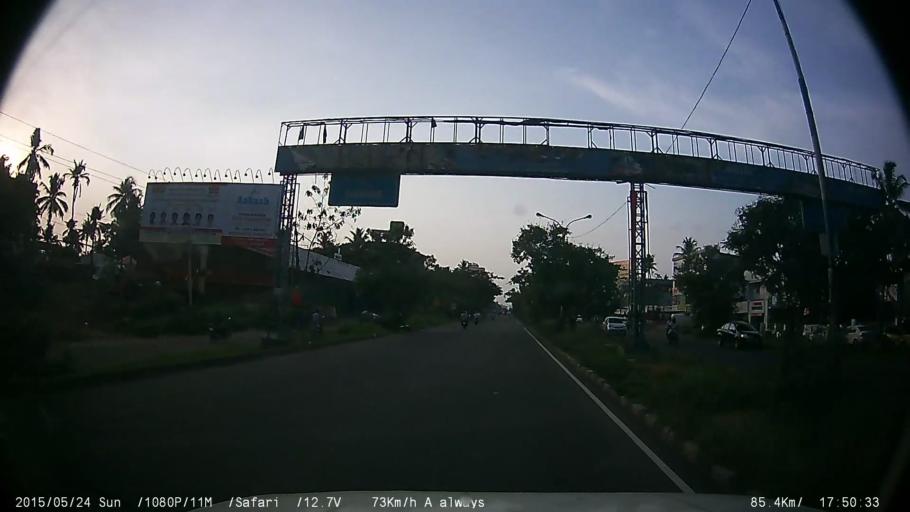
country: IN
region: Kerala
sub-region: Ernakulam
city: Elur
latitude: 9.9995
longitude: 76.3139
